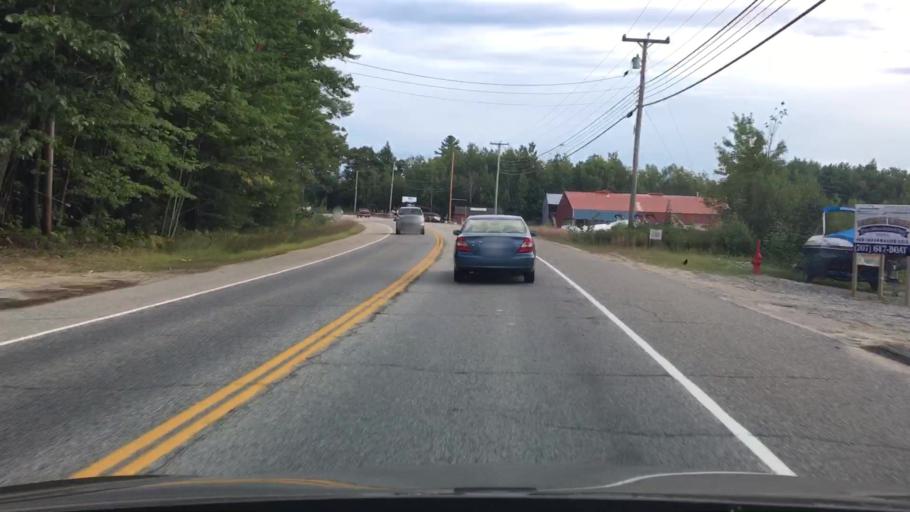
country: US
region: Maine
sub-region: Cumberland County
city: Bridgton
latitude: 44.0369
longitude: -70.6999
